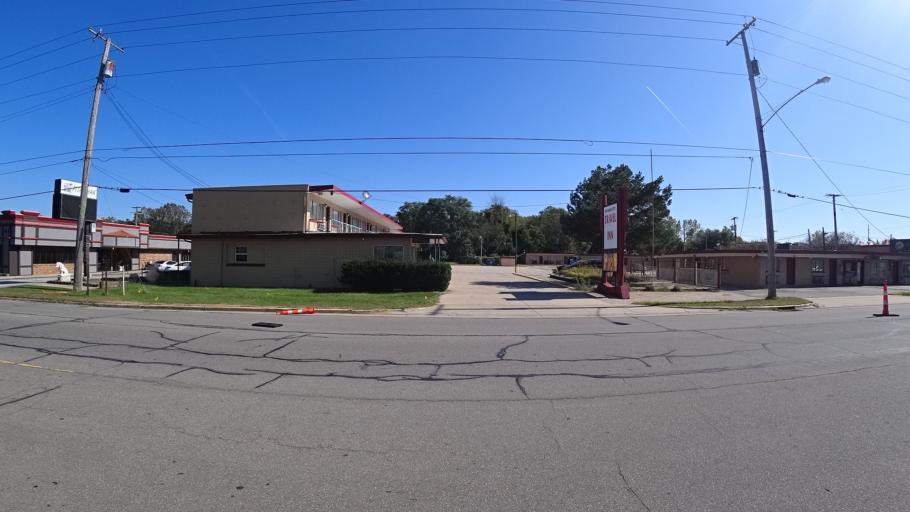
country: US
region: Indiana
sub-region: LaPorte County
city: Michigan City
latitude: 41.6821
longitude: -86.8940
